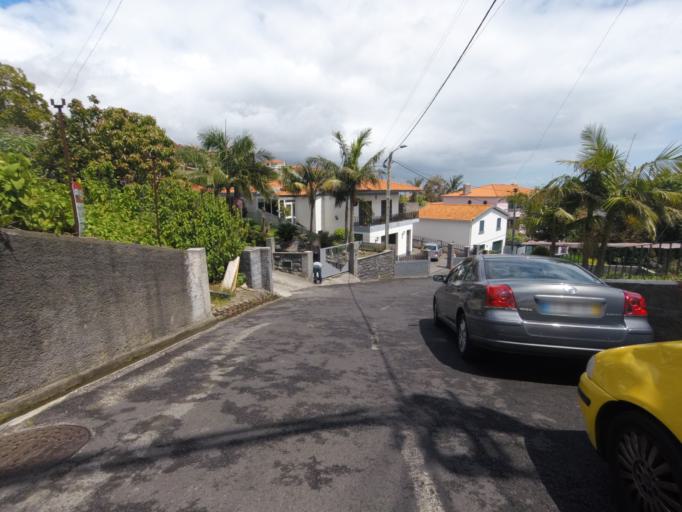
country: PT
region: Madeira
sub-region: Funchal
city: Nossa Senhora do Monte
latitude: 32.6735
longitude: -16.9221
